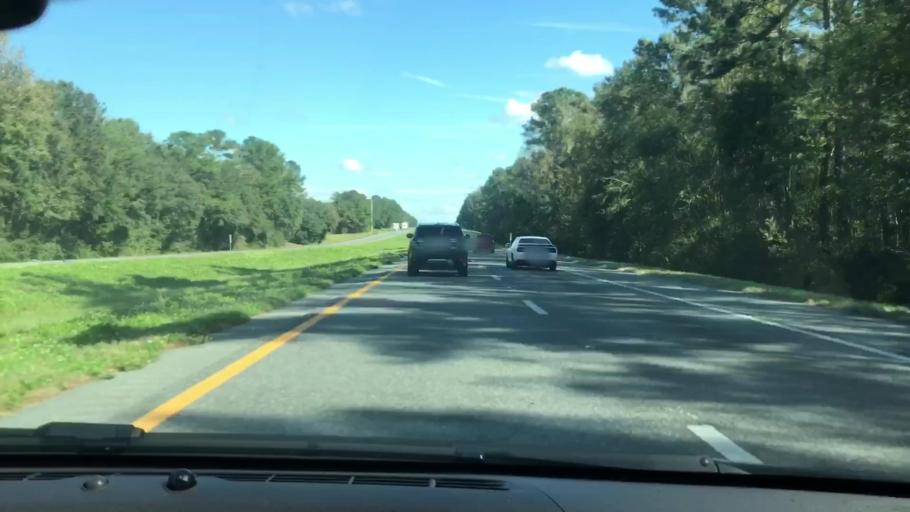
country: US
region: Florida
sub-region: Madison County
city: Madison
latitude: 30.4317
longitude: -83.5485
